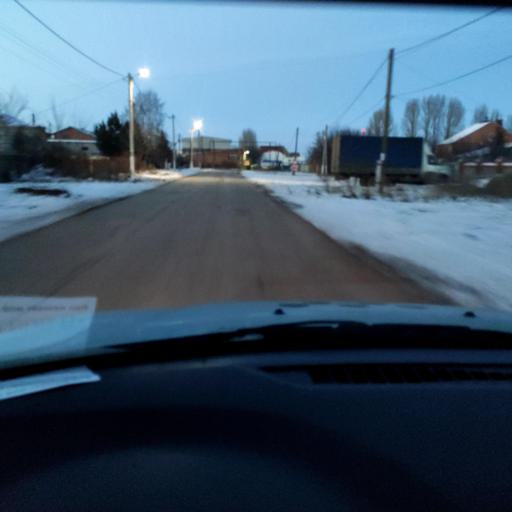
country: RU
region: Samara
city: Tol'yatti
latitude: 53.5680
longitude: 49.3905
